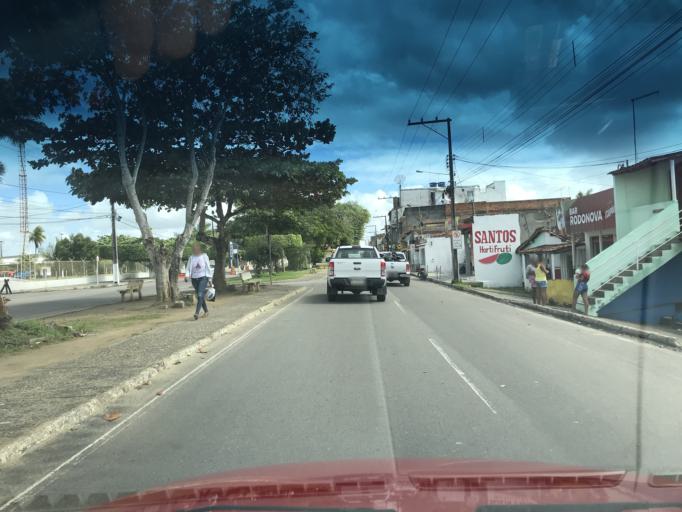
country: BR
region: Bahia
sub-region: Santo Antonio De Jesus
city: Santo Antonio de Jesus
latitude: -12.9793
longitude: -39.2788
